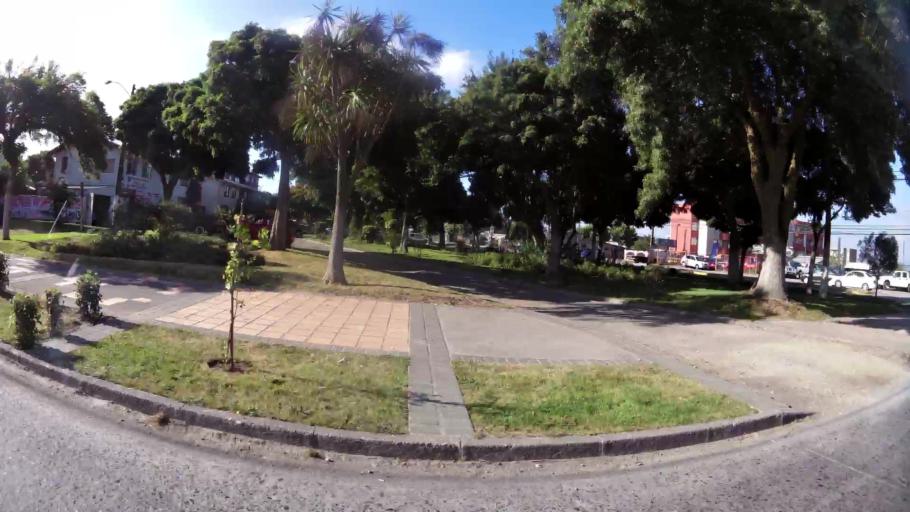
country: CL
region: Biobio
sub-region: Provincia de Concepcion
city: Concepcion
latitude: -36.7959
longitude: -73.0867
